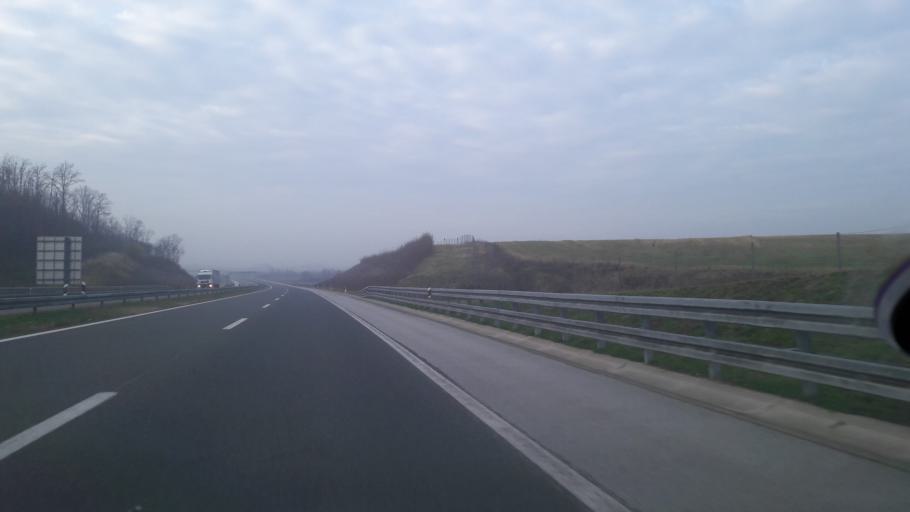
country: HR
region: Osjecko-Baranjska
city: Piskorevci
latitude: 45.3207
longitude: 18.3755
